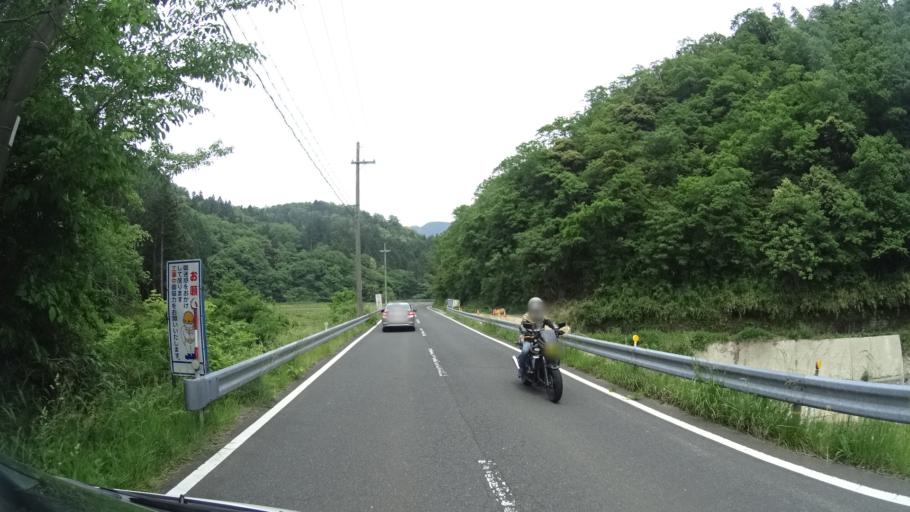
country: JP
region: Kyoto
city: Miyazu
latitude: 35.7116
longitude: 135.2610
